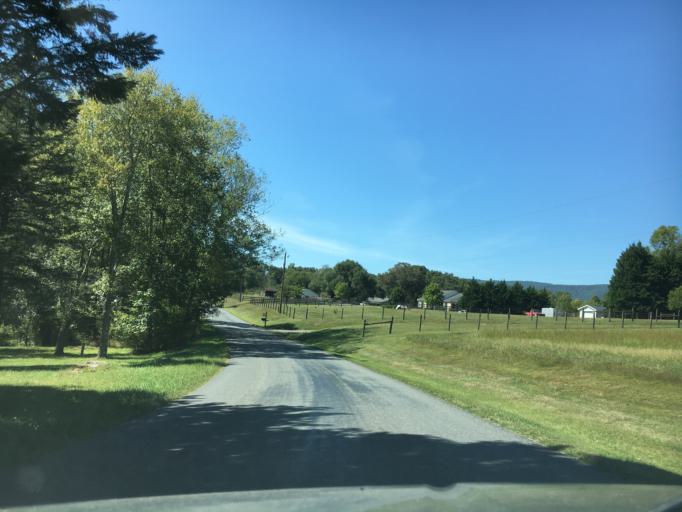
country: US
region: Virginia
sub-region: Albemarle County
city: Crozet
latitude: 38.0171
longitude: -78.7582
